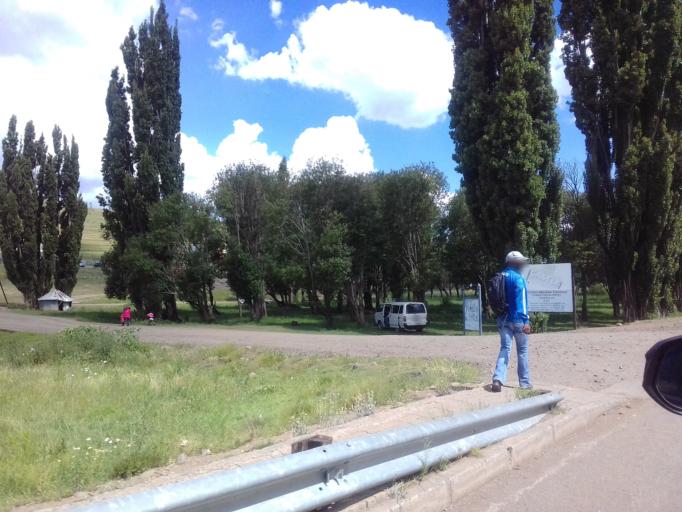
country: LS
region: Thaba-Tseka
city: Thaba-Tseka
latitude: -29.5223
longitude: 28.6030
